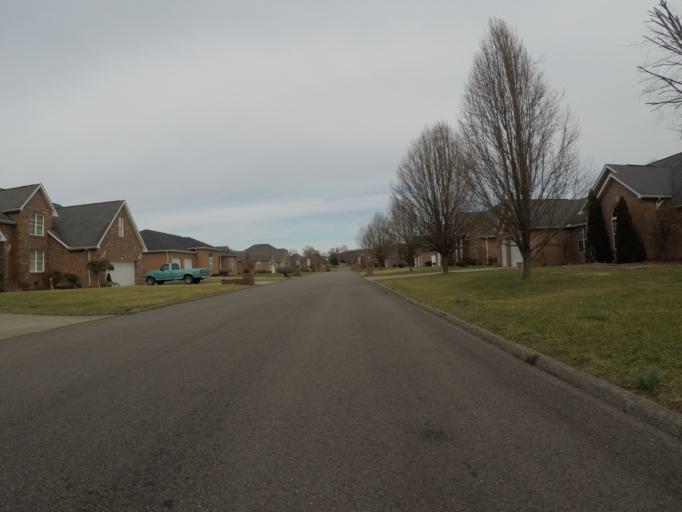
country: US
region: West Virginia
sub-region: Cabell County
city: Pea Ridge
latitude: 38.4453
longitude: -82.3486
